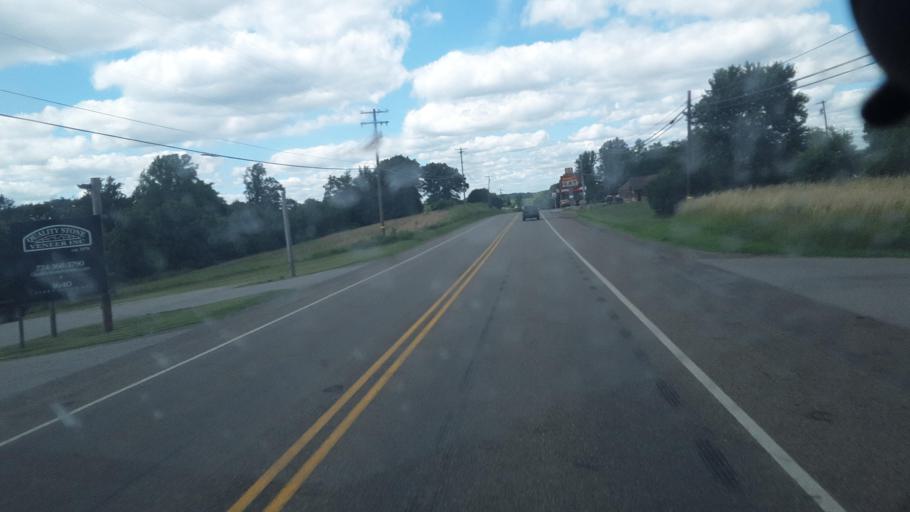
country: US
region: Pennsylvania
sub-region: Butler County
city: Prospect
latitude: 40.9485
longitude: -80.1538
